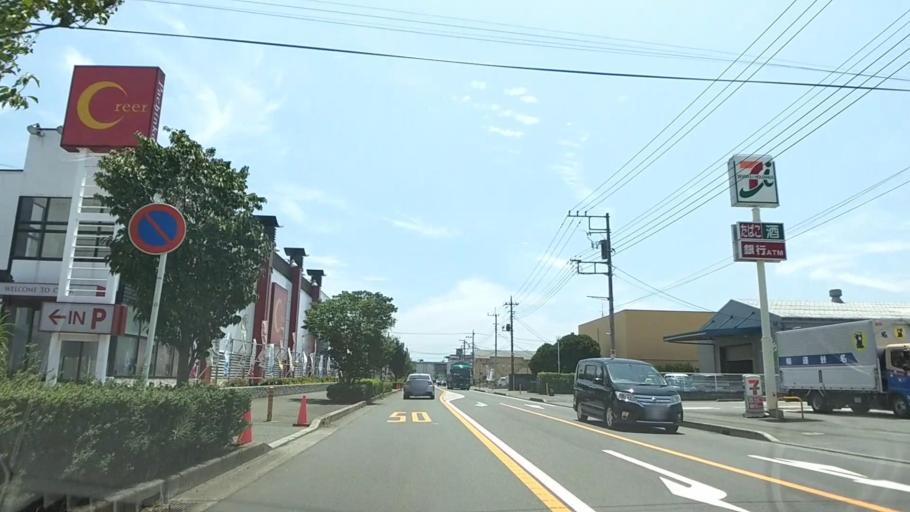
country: JP
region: Kanagawa
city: Atsugi
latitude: 35.3964
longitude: 139.3808
